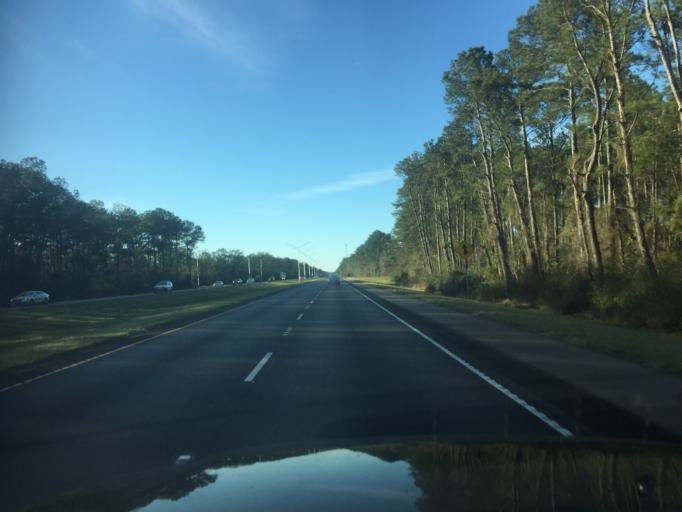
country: US
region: Louisiana
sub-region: Saint Tammany Parish
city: Lacombe
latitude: 30.3529
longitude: -89.9212
